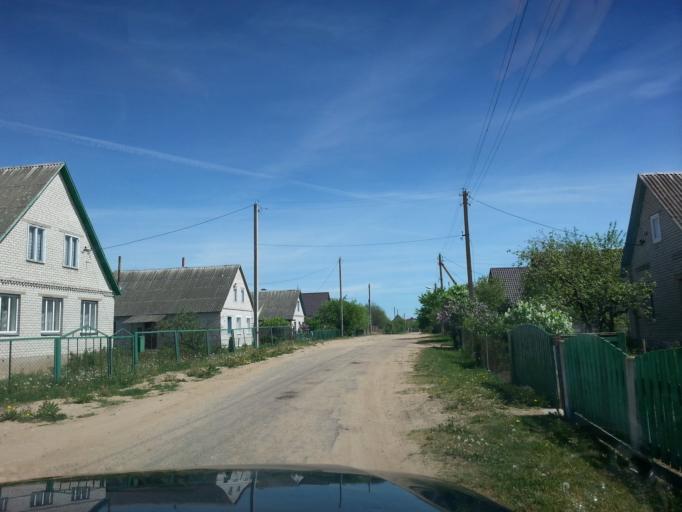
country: BY
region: Minsk
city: Narach
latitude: 54.9410
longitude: 26.6869
